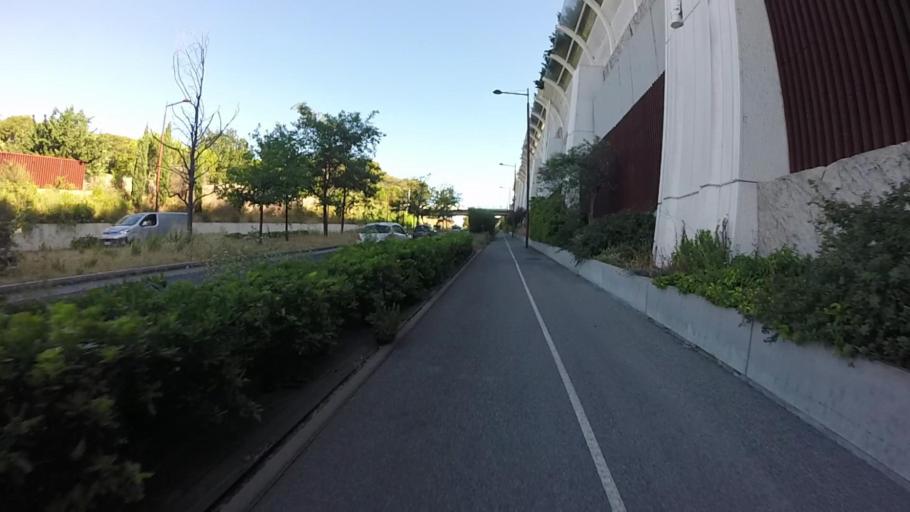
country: FR
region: Provence-Alpes-Cote d'Azur
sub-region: Departement des Alpes-Maritimes
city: Biot
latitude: 43.5925
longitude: 7.0921
